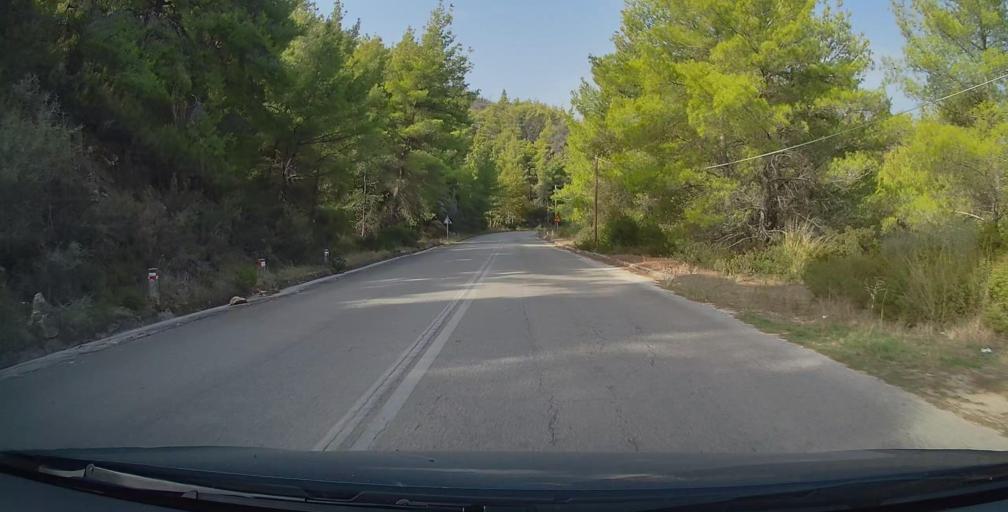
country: GR
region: Central Macedonia
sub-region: Nomos Chalkidikis
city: Sarti
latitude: 40.1141
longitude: 23.9796
